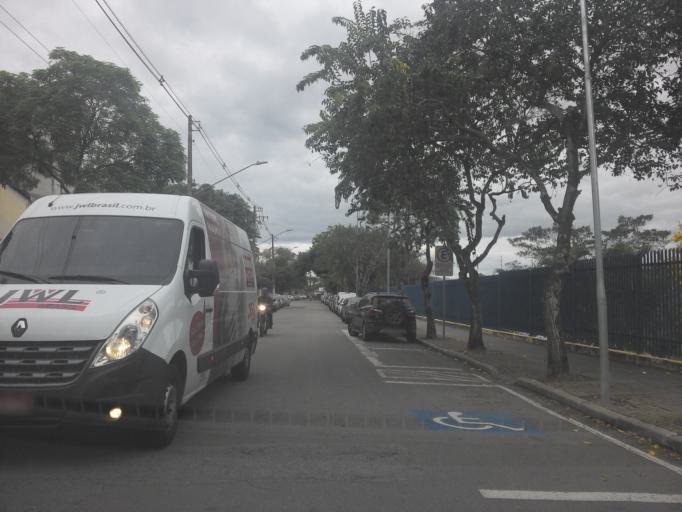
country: BR
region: Sao Paulo
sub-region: Sao Jose Dos Campos
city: Sao Jose dos Campos
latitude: -23.1846
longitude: -45.8787
